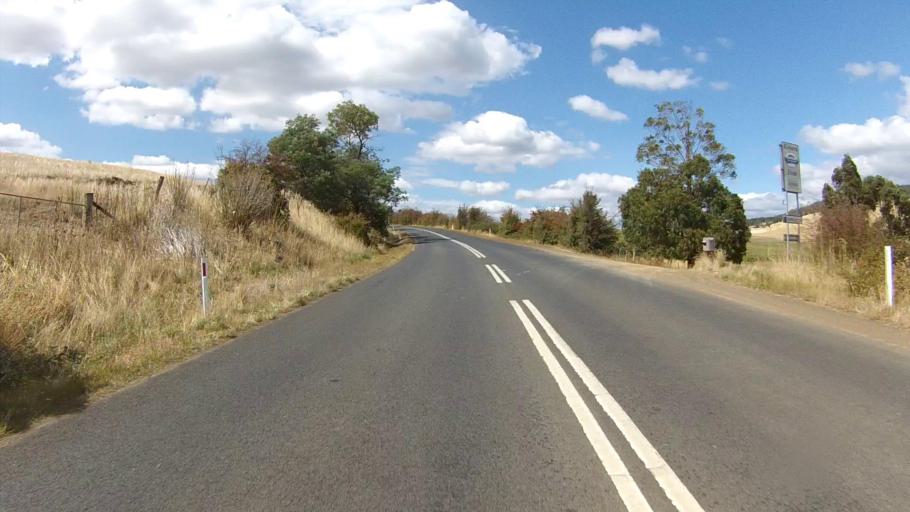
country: AU
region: Tasmania
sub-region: Derwent Valley
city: New Norfolk
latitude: -42.7365
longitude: 146.9295
